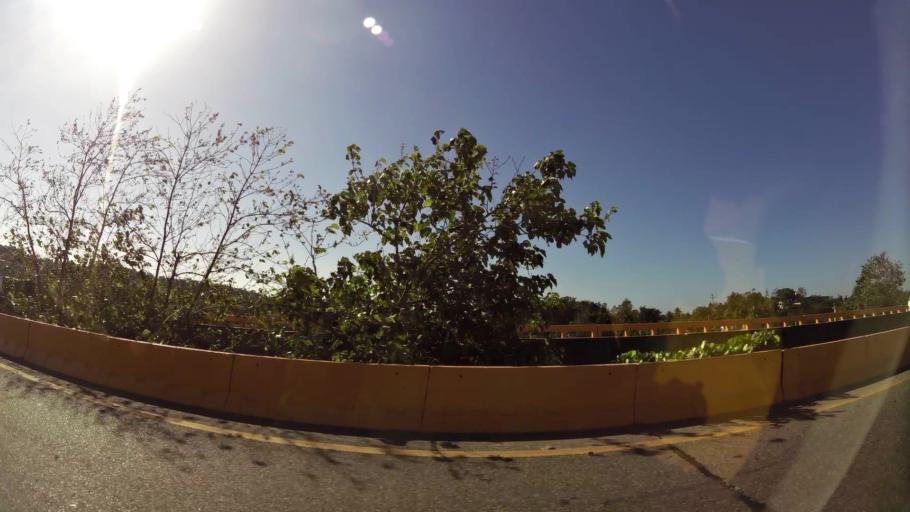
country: DO
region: San Cristobal
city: El Carril
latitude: 18.4393
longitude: -70.0081
